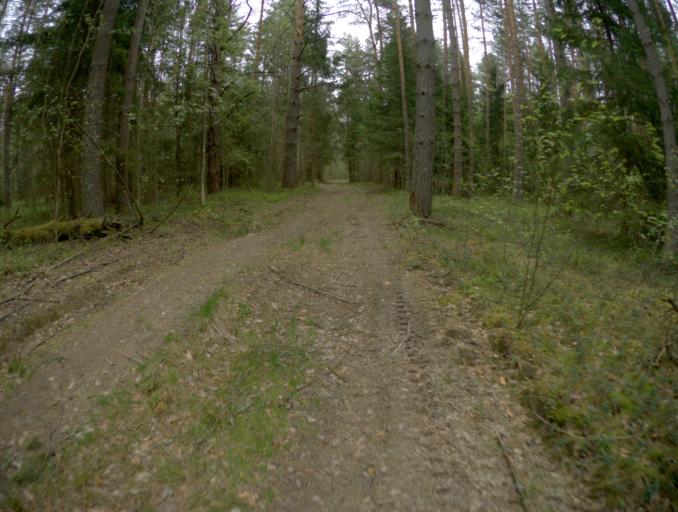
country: RU
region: Vladimir
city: Golovino
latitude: 55.9102
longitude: 40.4495
